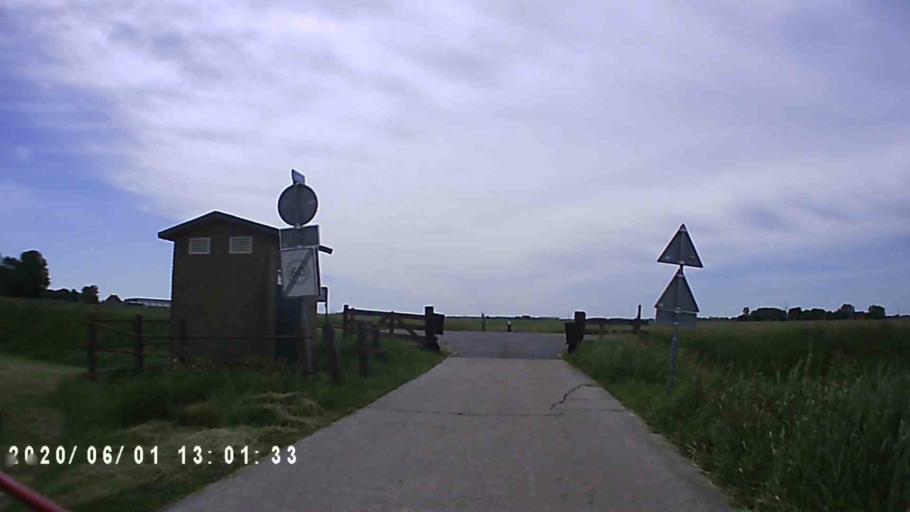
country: NL
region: Friesland
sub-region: Gemeente Franekeradeel
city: Tzum
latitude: 53.1443
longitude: 5.5390
